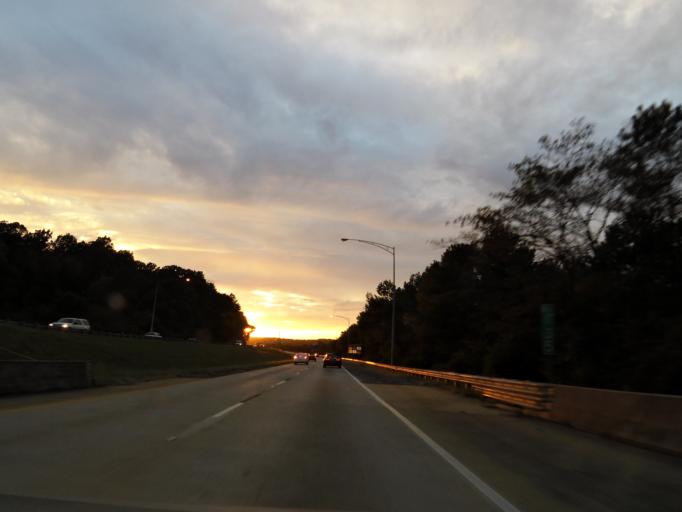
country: US
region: Alabama
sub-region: Jefferson County
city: Irondale
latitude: 33.5867
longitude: -86.6863
